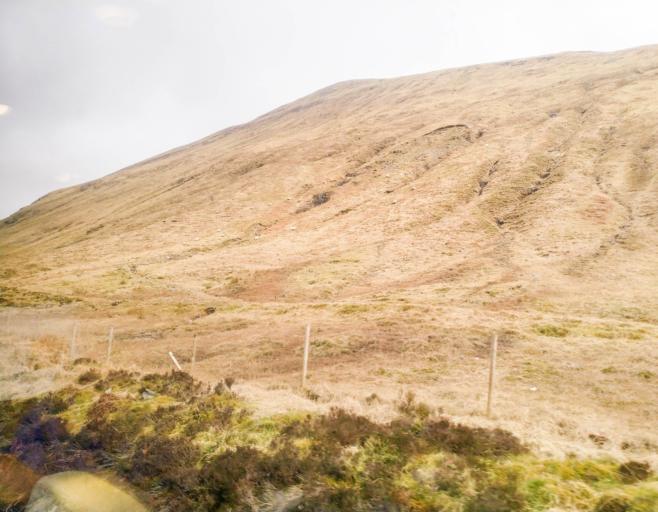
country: GB
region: Scotland
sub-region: Argyll and Bute
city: Garelochhead
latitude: 56.4562
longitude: -4.7116
